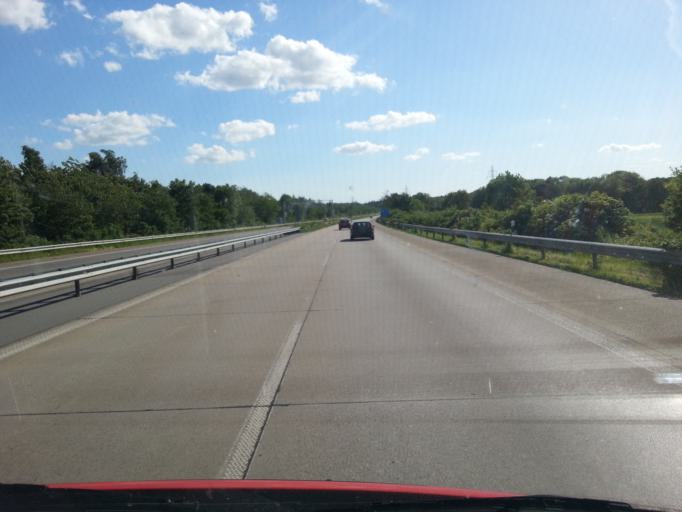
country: DE
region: Schleswig-Holstein
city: Sierksdorf
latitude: 54.0641
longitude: 10.7506
